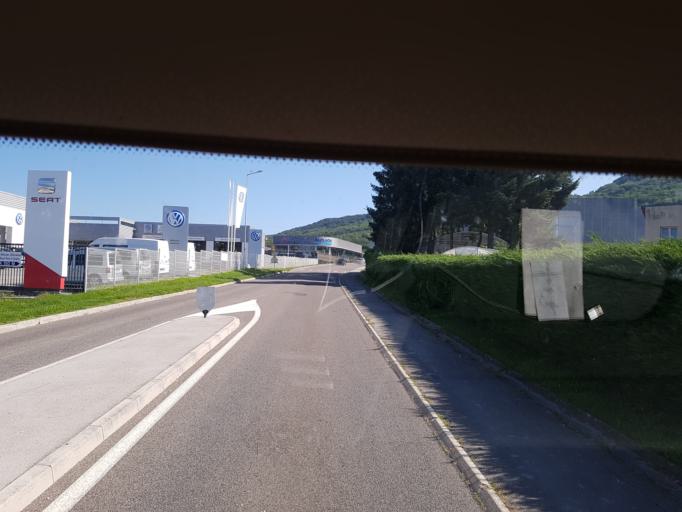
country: FR
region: Franche-Comte
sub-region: Departement du Jura
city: Perrigny
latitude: 46.6740
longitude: 5.5811
